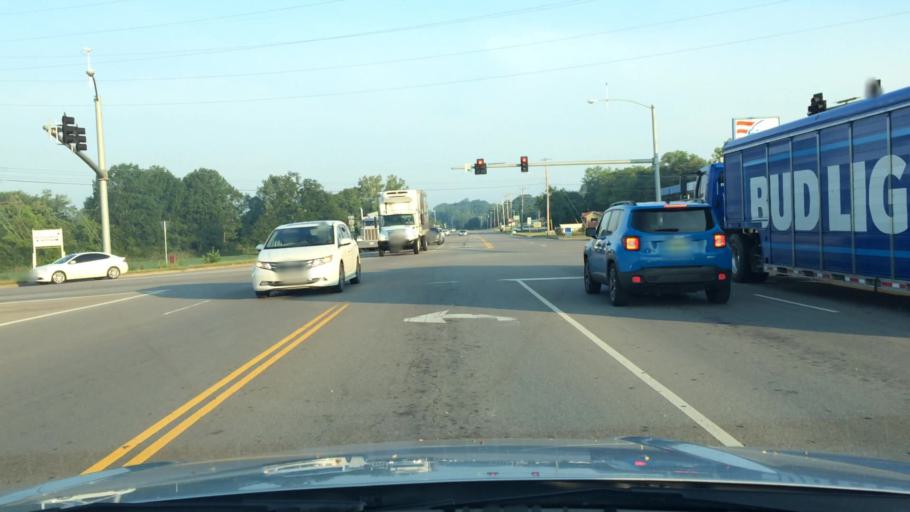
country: US
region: Tennessee
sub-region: Giles County
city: Pulaski
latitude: 35.2048
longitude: -87.0624
